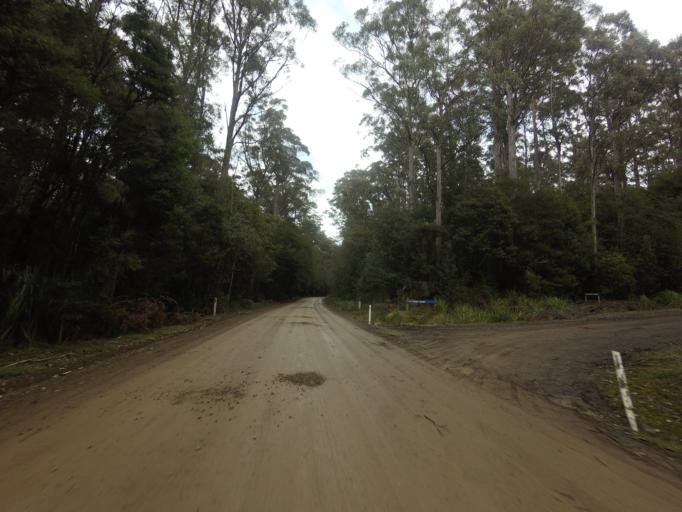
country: AU
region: Tasmania
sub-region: Huon Valley
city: Geeveston
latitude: -43.4151
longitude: 146.8901
